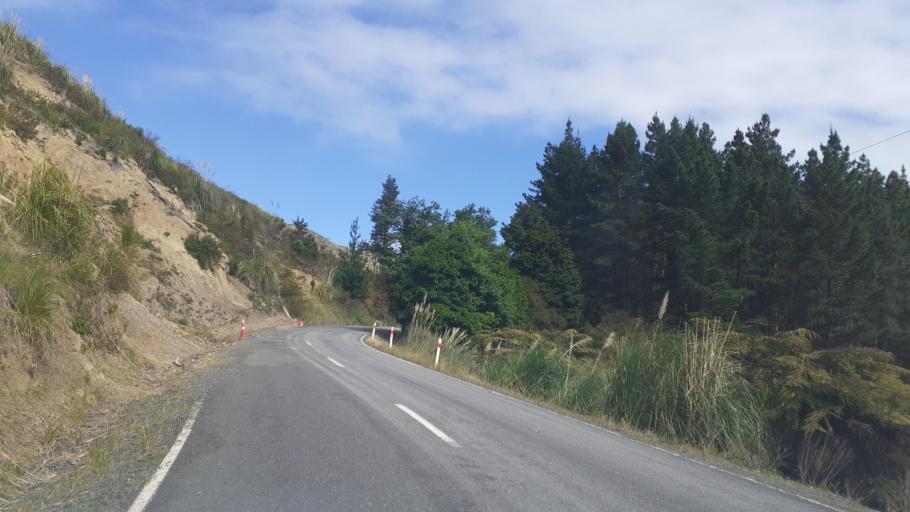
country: NZ
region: Northland
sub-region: Far North District
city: Moerewa
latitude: -35.5355
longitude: 173.9585
